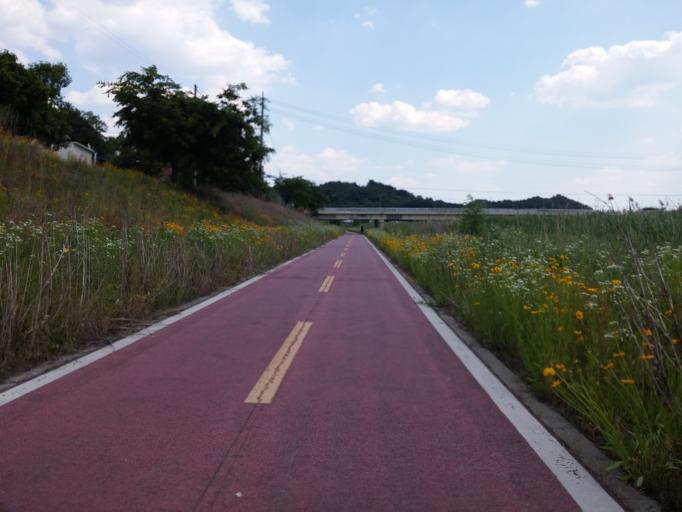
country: KR
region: Chungcheongbuk-do
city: Cheongju-si
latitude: 36.5656
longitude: 127.5086
